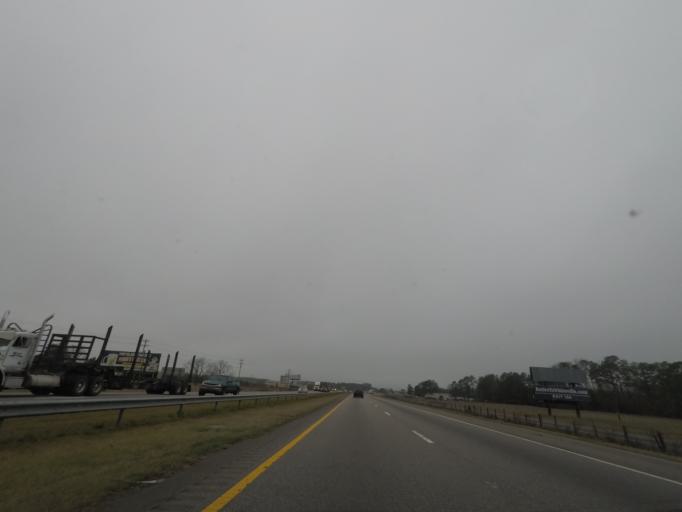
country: US
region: North Carolina
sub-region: Robeson County
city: Lumberton
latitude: 34.6190
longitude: -79.0638
